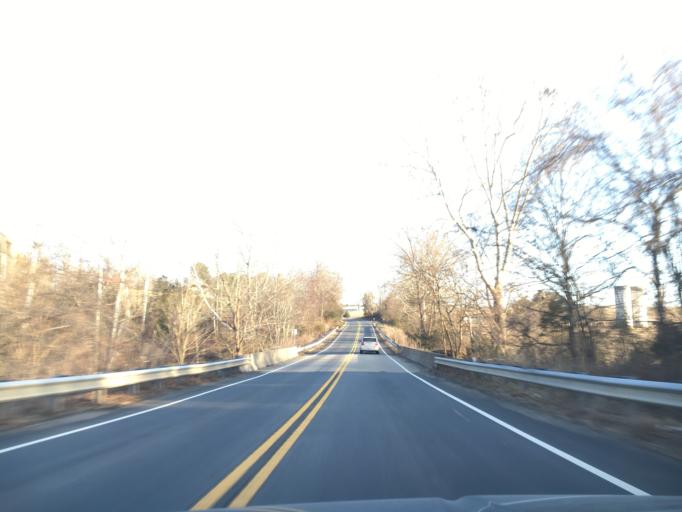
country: US
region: Virginia
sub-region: Culpeper County
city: Merrimac
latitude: 38.5252
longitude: -78.1153
